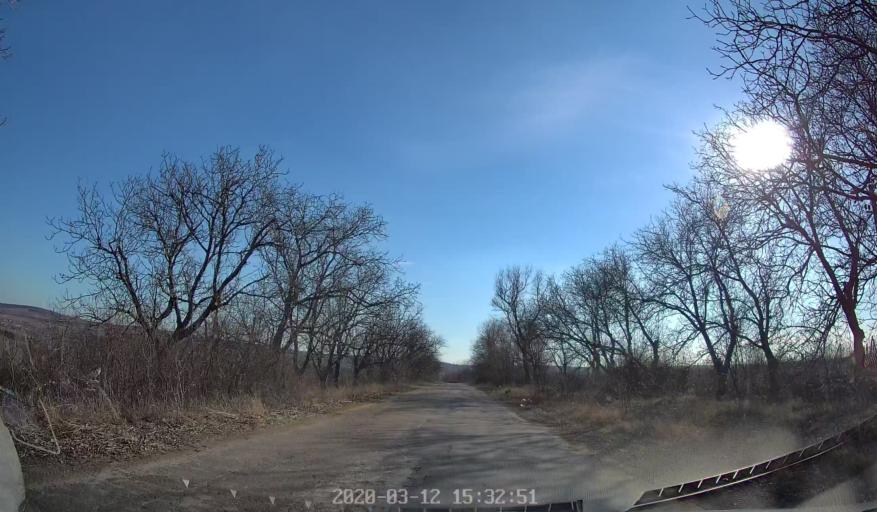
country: MD
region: Chisinau
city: Ciorescu
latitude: 47.1482
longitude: 28.9393
